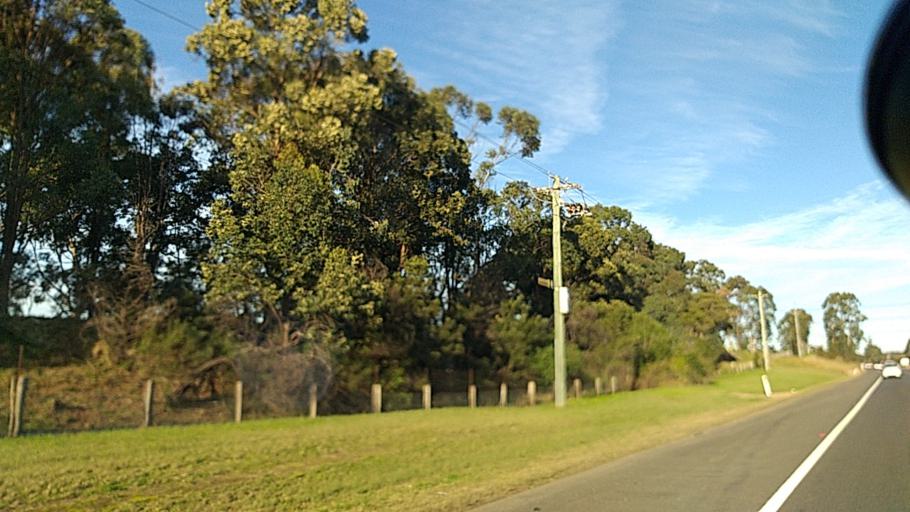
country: AU
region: New South Wales
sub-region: Hawkesbury
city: South Windsor
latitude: -33.6726
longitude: 150.8075
